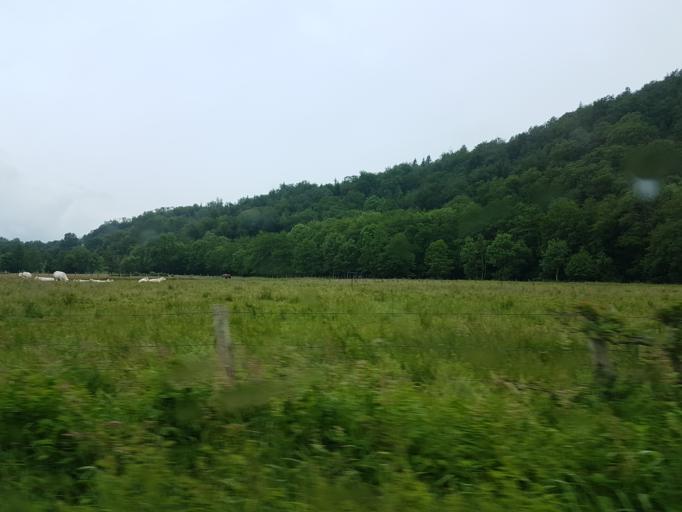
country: FR
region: Bourgogne
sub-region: Departement de la Nievre
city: Lormes
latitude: 47.1788
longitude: 3.7802
